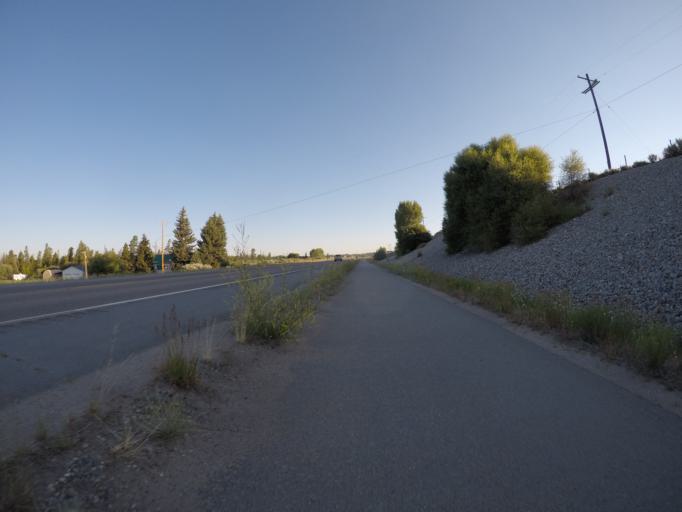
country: US
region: Wyoming
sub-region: Sublette County
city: Pinedale
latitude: 42.8492
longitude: -109.8492
